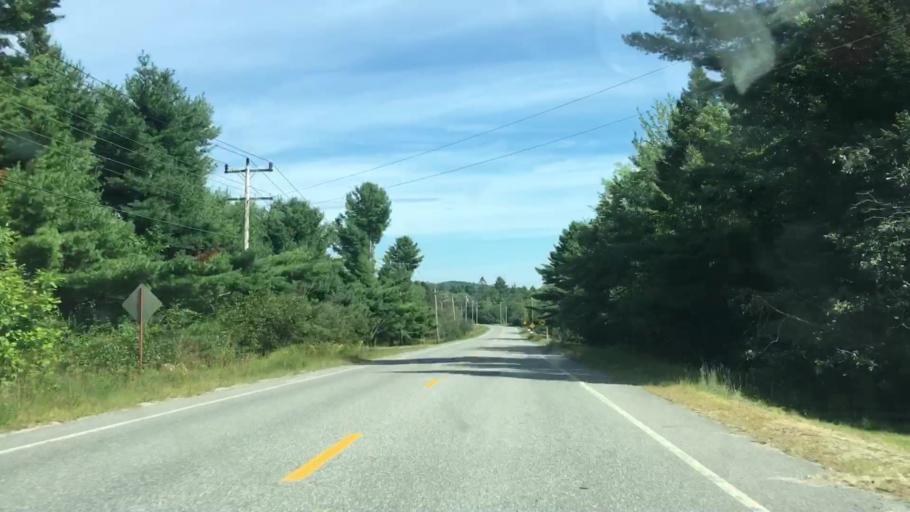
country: US
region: Maine
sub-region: Penobscot County
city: Lincoln
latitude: 45.3933
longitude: -68.5247
